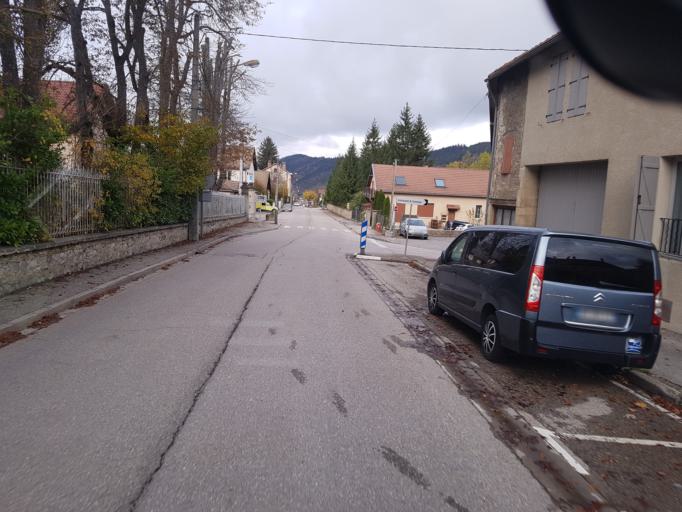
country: FR
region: Rhone-Alpes
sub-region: Departement de l'Isere
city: La Motte-Saint-Martin
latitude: 44.9117
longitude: 5.6321
